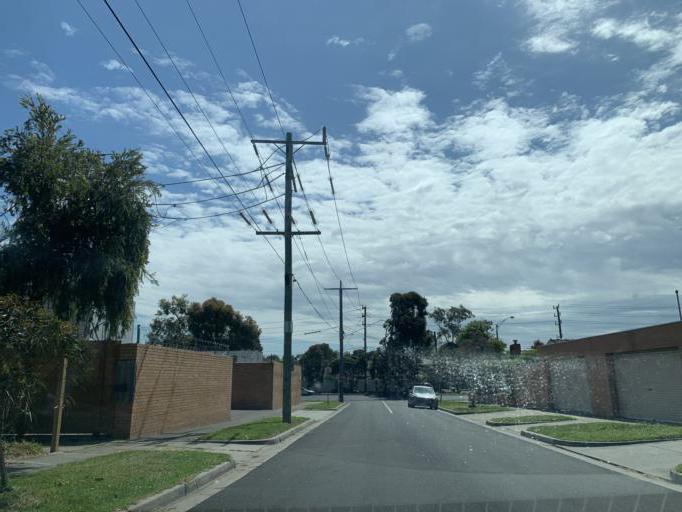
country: AU
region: Victoria
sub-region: Bayside
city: Hampton East
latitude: -37.9331
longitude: 145.0293
